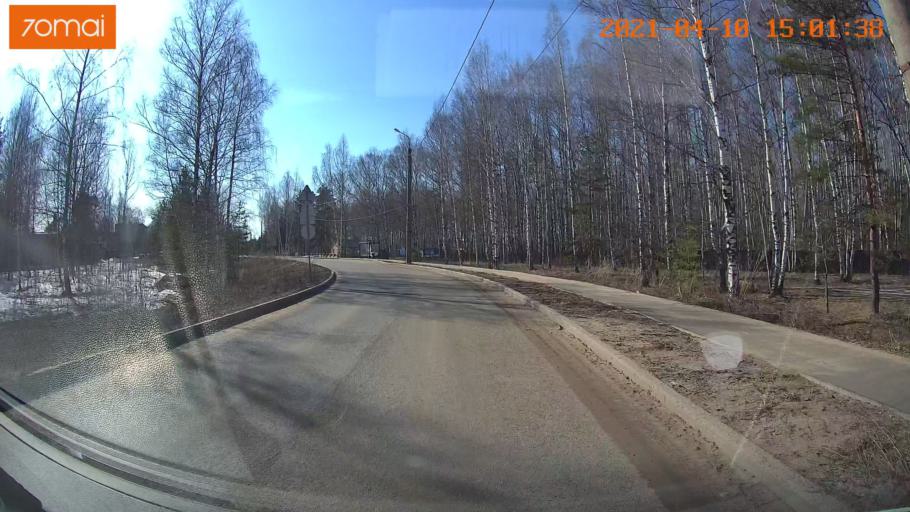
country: RU
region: Ivanovo
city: Bogorodskoye
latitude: 56.9983
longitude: 41.0547
